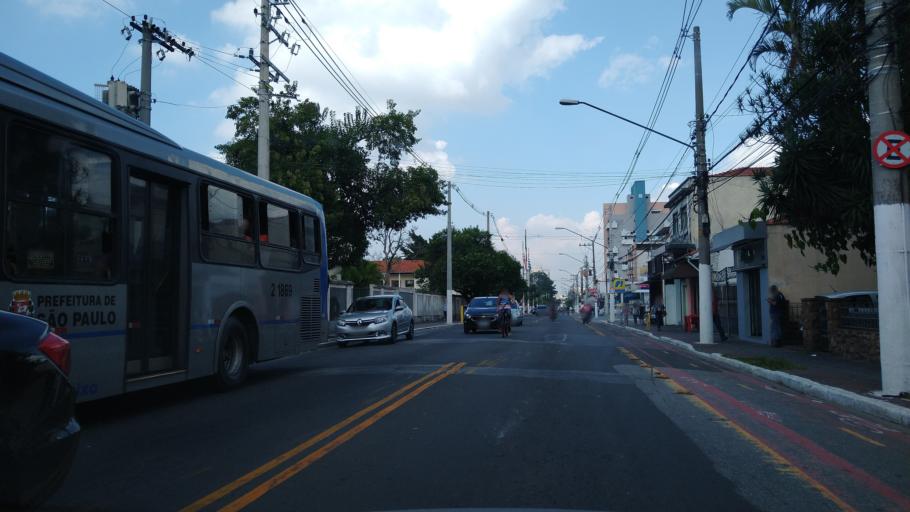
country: BR
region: Sao Paulo
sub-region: Guarulhos
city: Guarulhos
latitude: -23.4678
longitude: -46.5838
